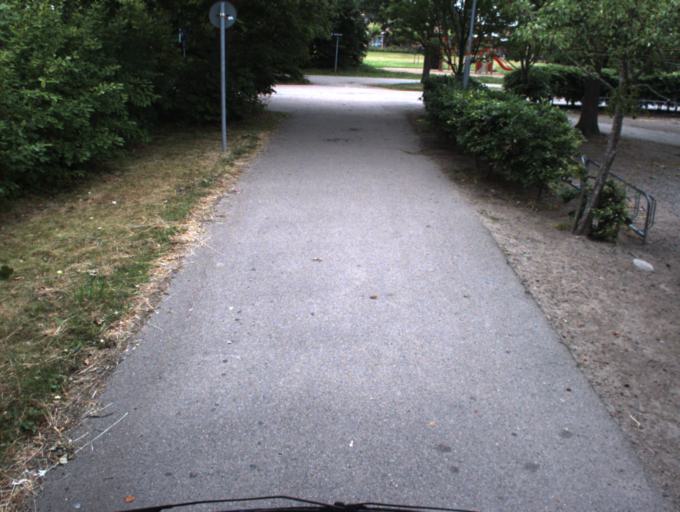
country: SE
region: Skane
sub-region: Helsingborg
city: Rydeback
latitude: 56.0101
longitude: 12.7578
